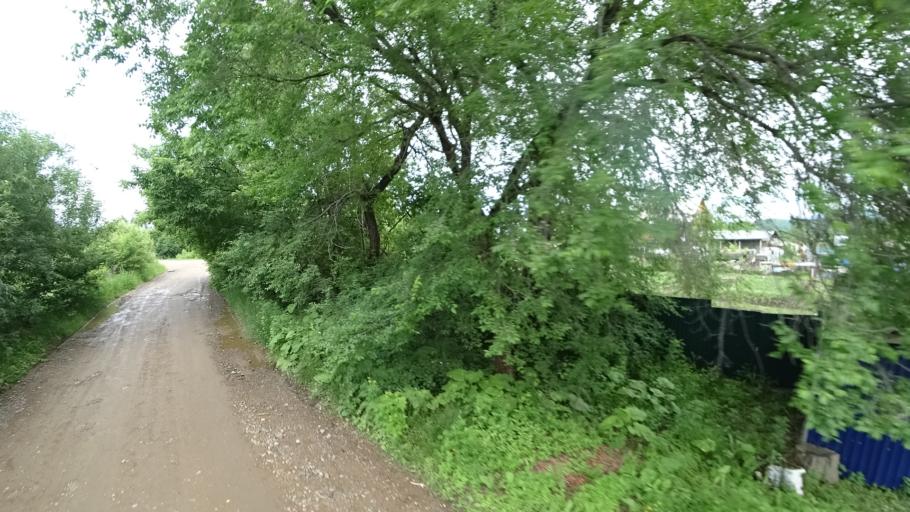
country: RU
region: Primorskiy
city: Novosysoyevka
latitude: 44.2297
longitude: 133.3666
